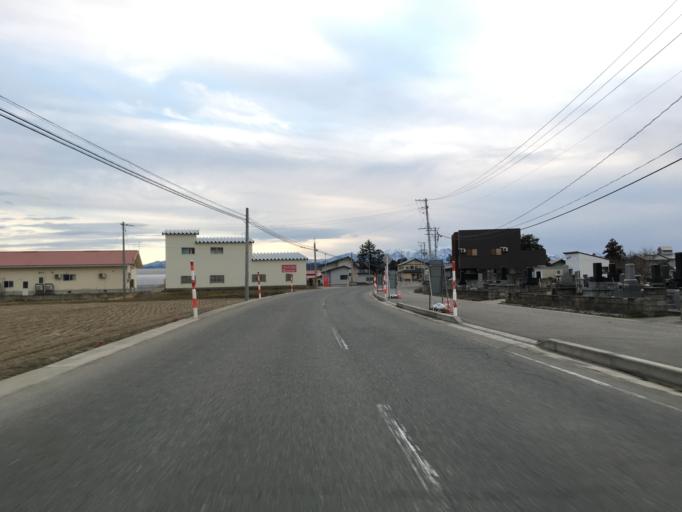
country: JP
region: Yamagata
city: Yonezawa
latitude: 37.9940
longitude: 140.0774
